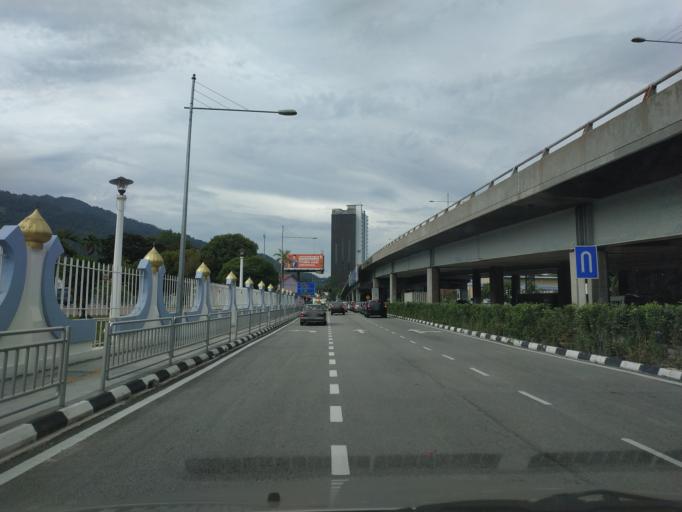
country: MY
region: Penang
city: George Town
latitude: 5.4068
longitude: 100.3029
